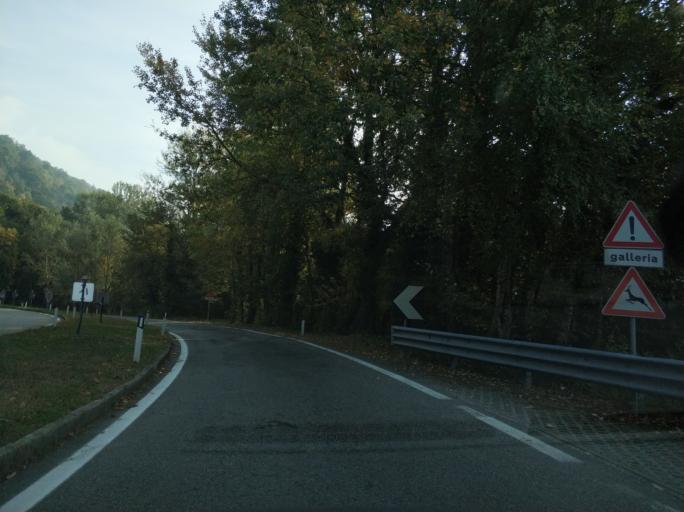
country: IT
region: Piedmont
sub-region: Provincia di Biella
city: Donato
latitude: 45.5137
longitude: 7.9018
